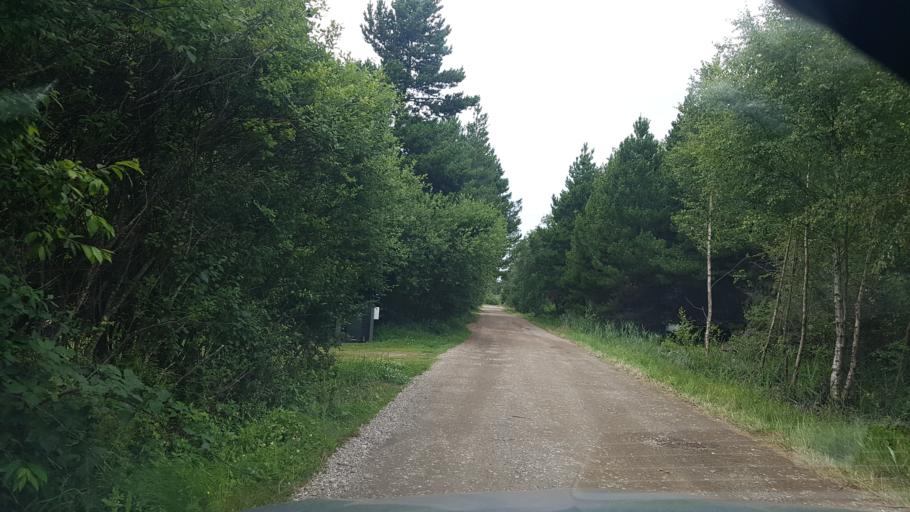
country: DE
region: Schleswig-Holstein
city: List
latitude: 55.0900
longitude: 8.5293
